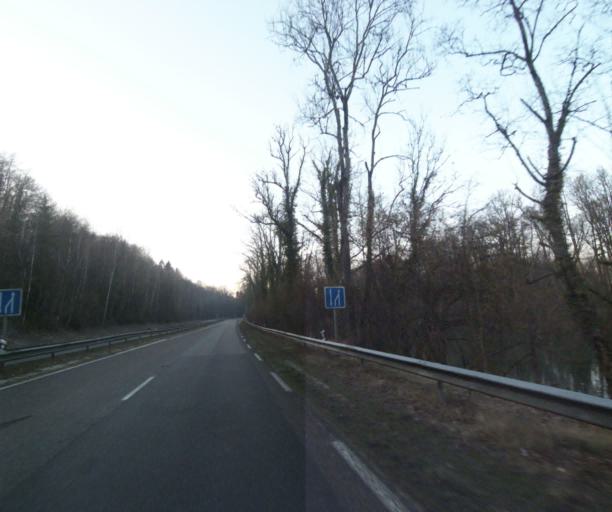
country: FR
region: Lorraine
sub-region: Departement de la Meuse
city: Ancerville
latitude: 48.6121
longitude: 5.0031
